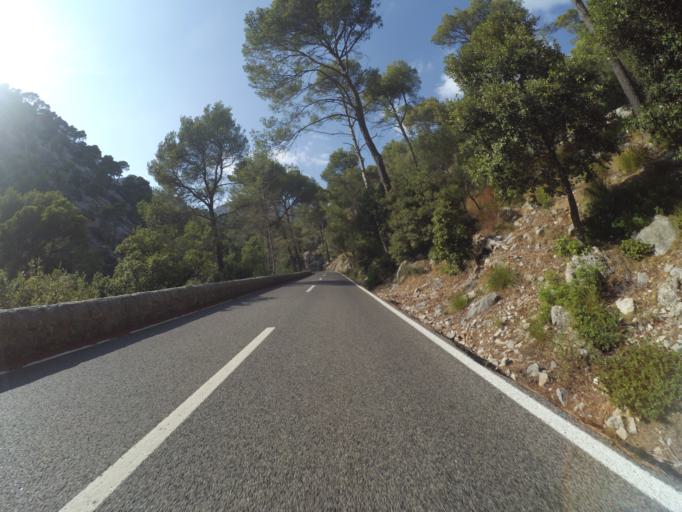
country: ES
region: Balearic Islands
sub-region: Illes Balears
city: Selva
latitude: 39.7852
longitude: 2.8955
